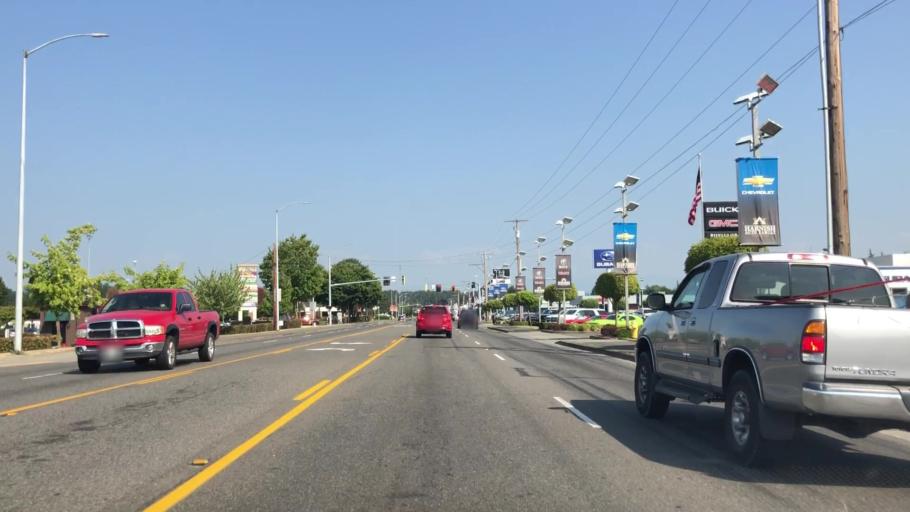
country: US
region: Washington
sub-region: Pierce County
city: Puyallup
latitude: 47.2013
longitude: -122.3038
